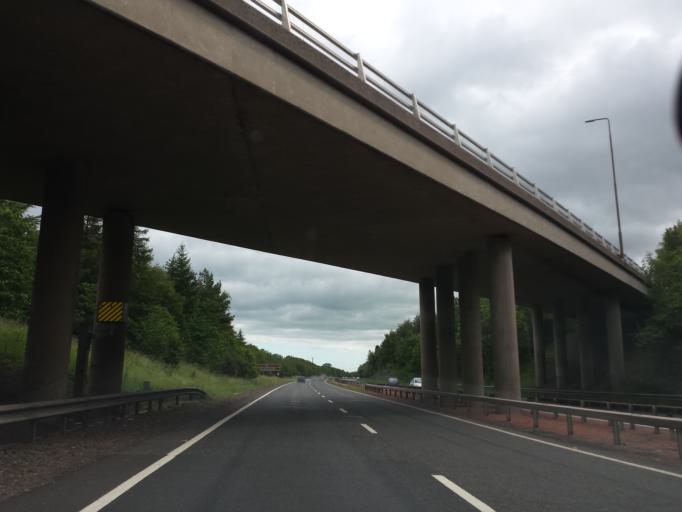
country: GB
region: Scotland
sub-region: East Lothian
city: Prestonpans
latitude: 55.9446
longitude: -2.9860
